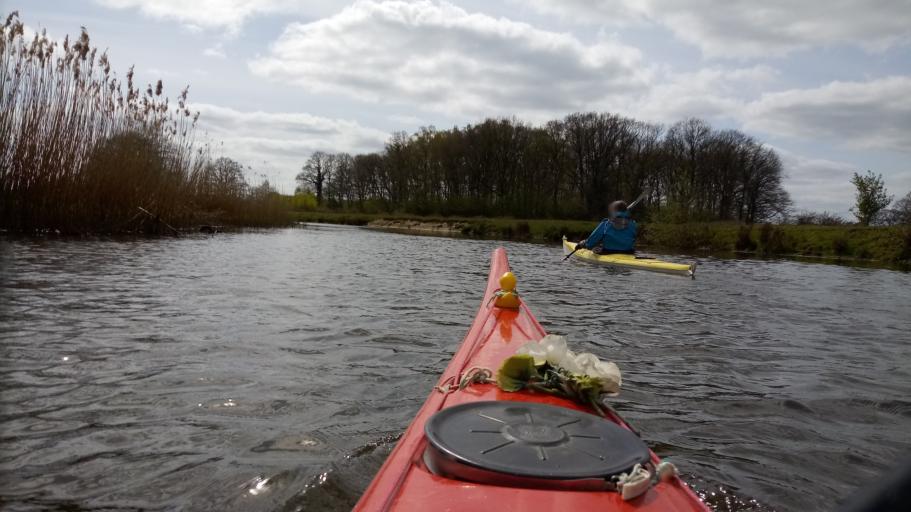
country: NL
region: Overijssel
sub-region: Gemeente Twenterand
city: Den Ham
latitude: 52.4628
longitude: 6.4469
